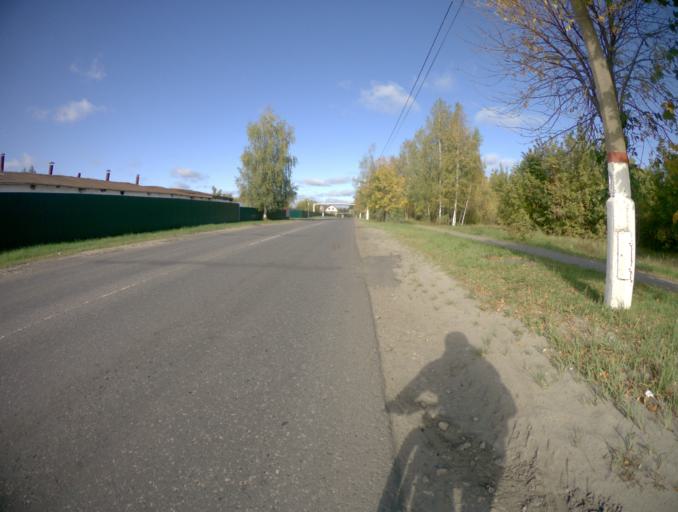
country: RU
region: Moskovskaya
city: Roshal'
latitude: 55.6612
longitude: 39.8747
